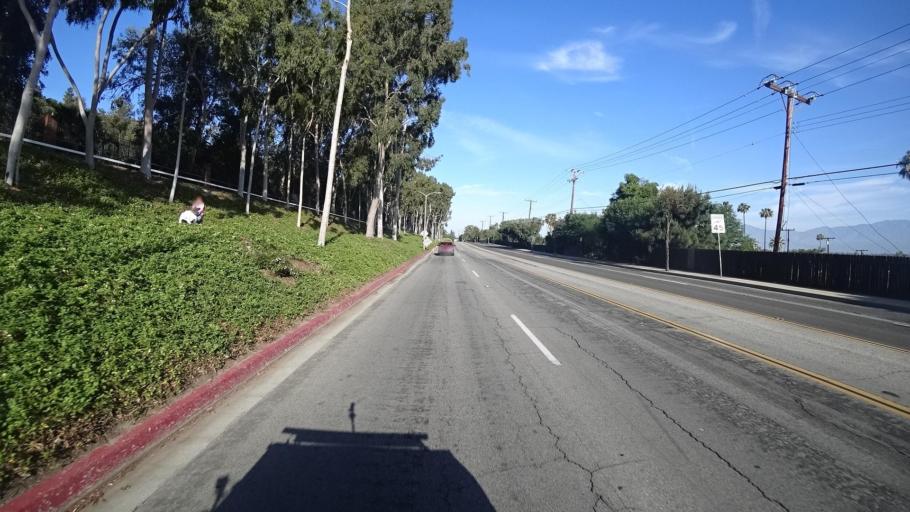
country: US
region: California
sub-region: Los Angeles County
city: La Puente
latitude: 34.0268
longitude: -117.9287
